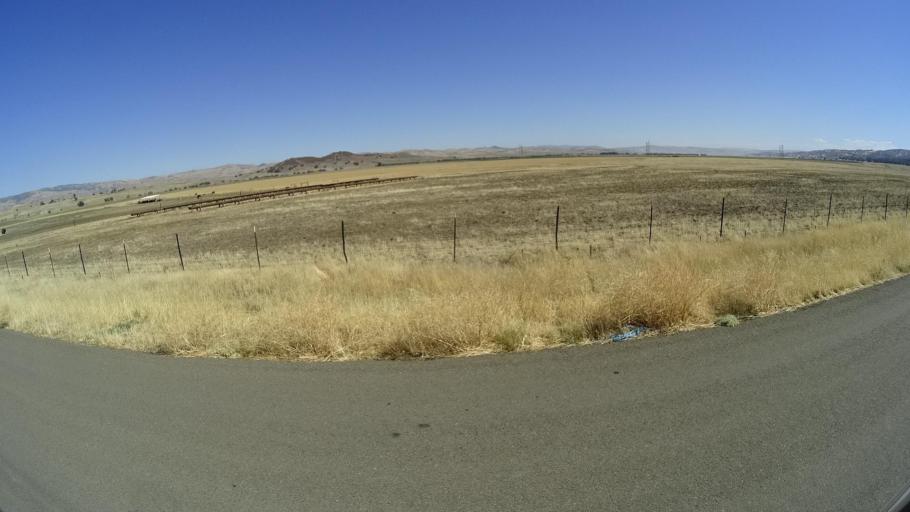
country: US
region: California
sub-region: San Luis Obispo County
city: Shandon
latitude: 35.8286
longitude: -120.3858
